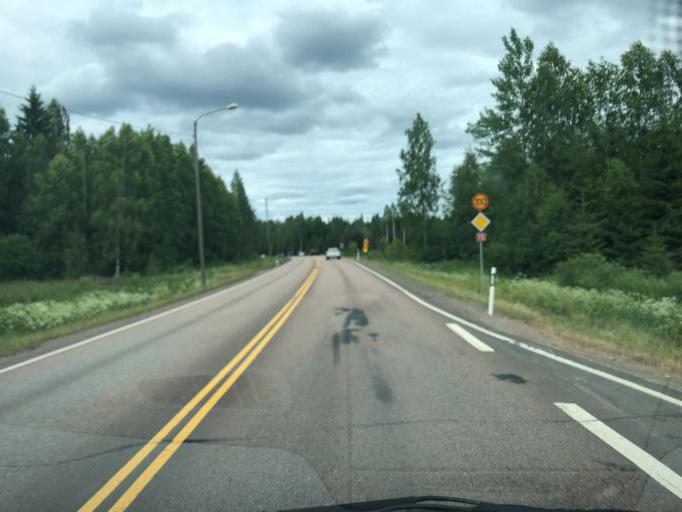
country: FI
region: Kymenlaakso
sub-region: Kouvola
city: Kouvola
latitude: 61.0283
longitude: 26.9834
